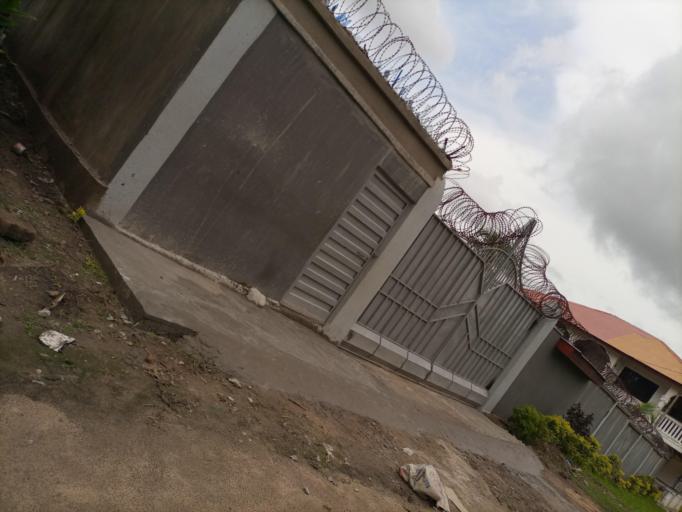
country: SL
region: Southern Province
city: Bo
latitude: 7.9531
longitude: -11.7463
